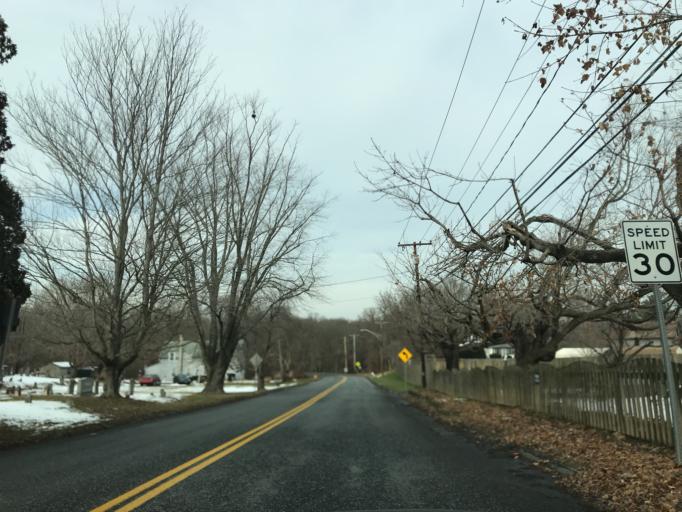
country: US
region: Maryland
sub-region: Harford County
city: Perryman
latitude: 39.4745
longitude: -76.2031
